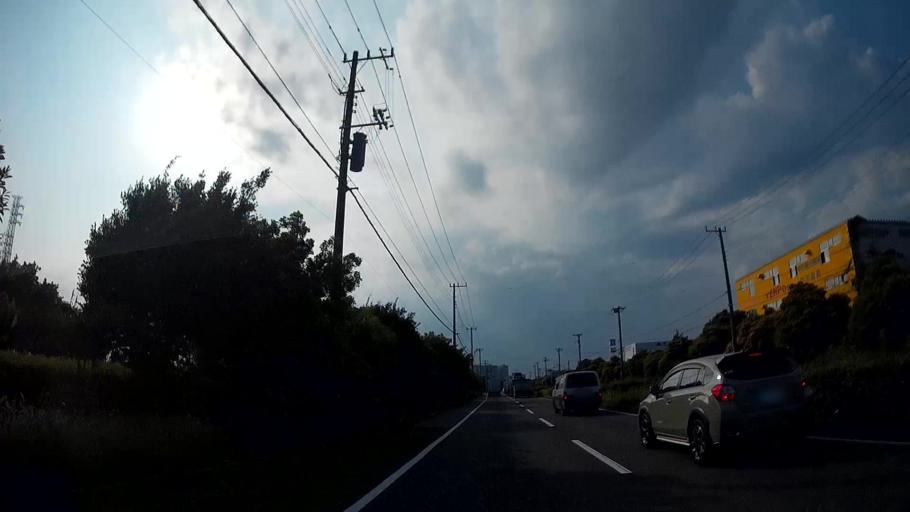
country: JP
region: Chiba
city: Funabashi
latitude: 35.6692
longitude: 140.0040
